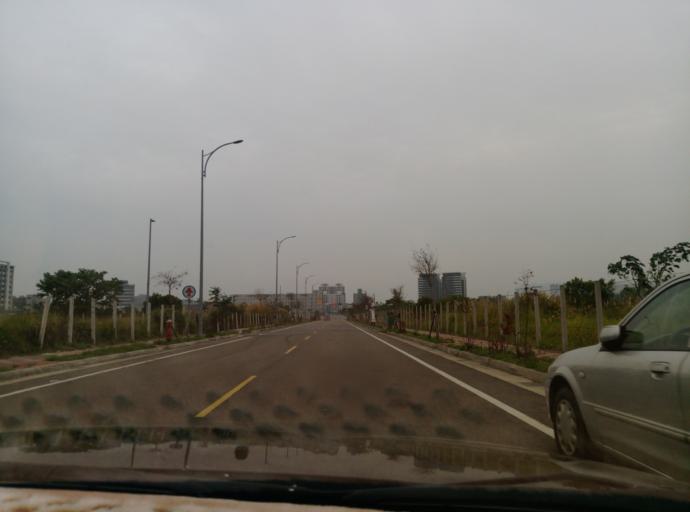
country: TW
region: Taiwan
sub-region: Hsinchu
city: Hsinchu
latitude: 24.7037
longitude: 120.9062
